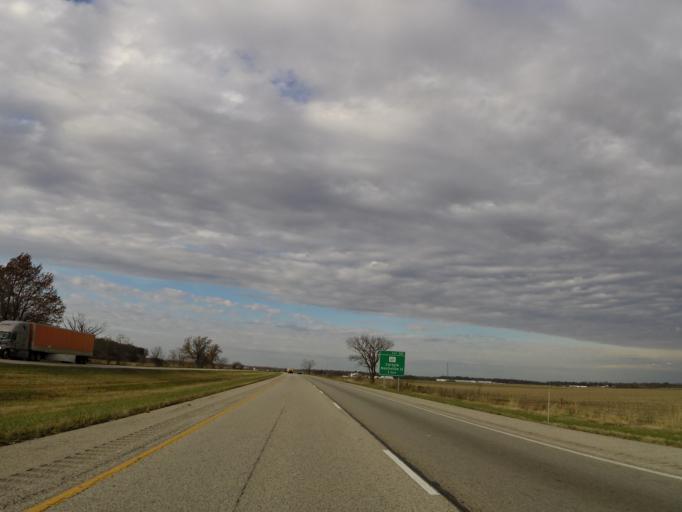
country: US
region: Illinois
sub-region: Washington County
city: Nashville
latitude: 38.3914
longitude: -89.3459
